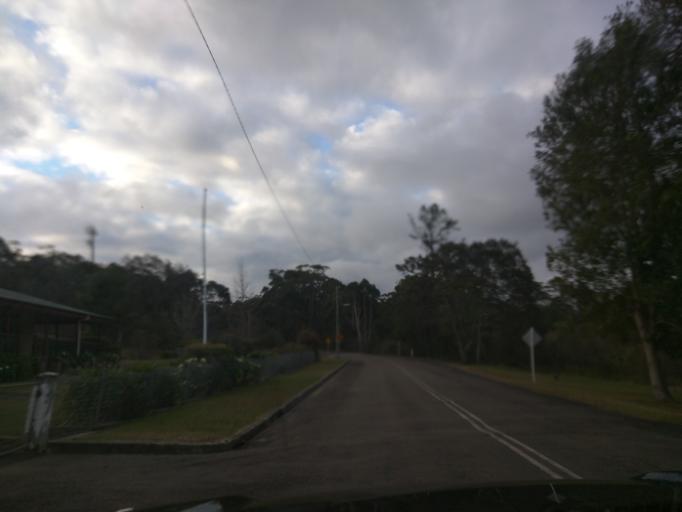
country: AU
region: New South Wales
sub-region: Wollongong
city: Mount Keira
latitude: -34.3249
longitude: 150.7463
